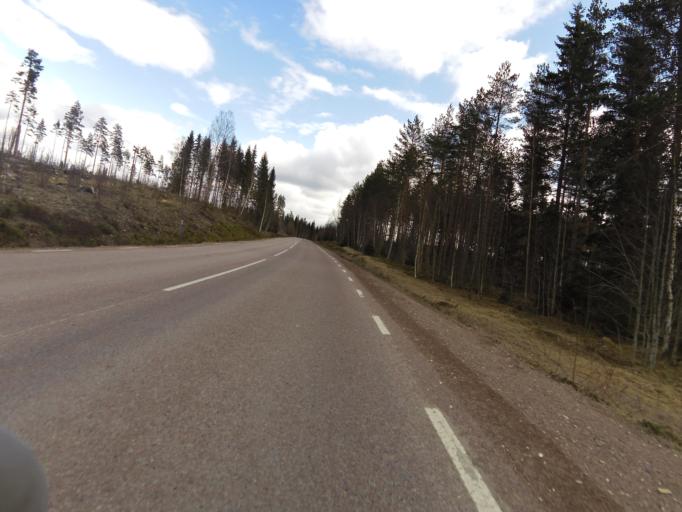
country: SE
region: Dalarna
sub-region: Avesta Kommun
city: Avesta
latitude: 60.3098
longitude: 16.2267
